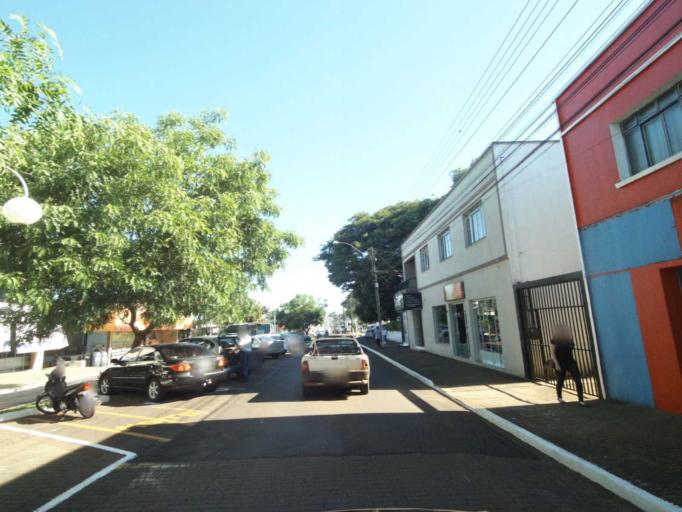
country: BR
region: Parana
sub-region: Coronel Vivida
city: Coronel Vivida
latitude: -25.9641
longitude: -52.8150
